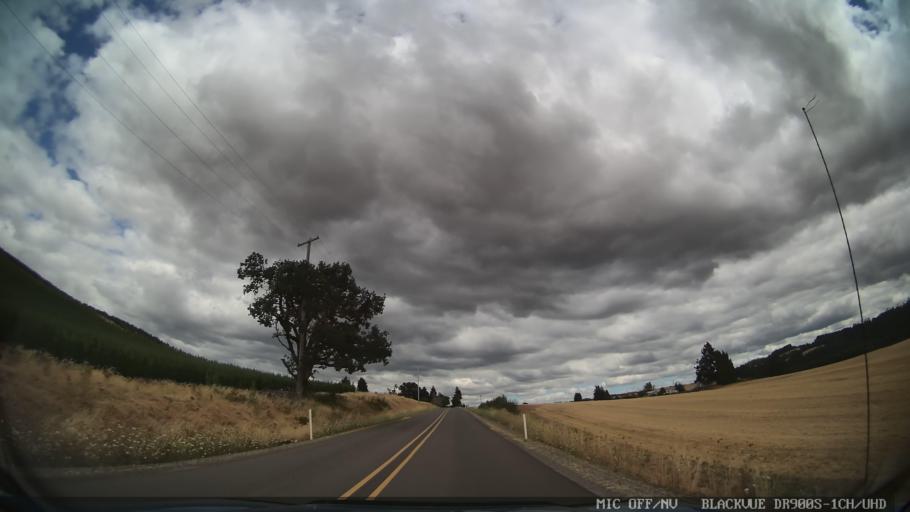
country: US
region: Oregon
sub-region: Marion County
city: Sublimity
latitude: 44.8724
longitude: -122.7311
